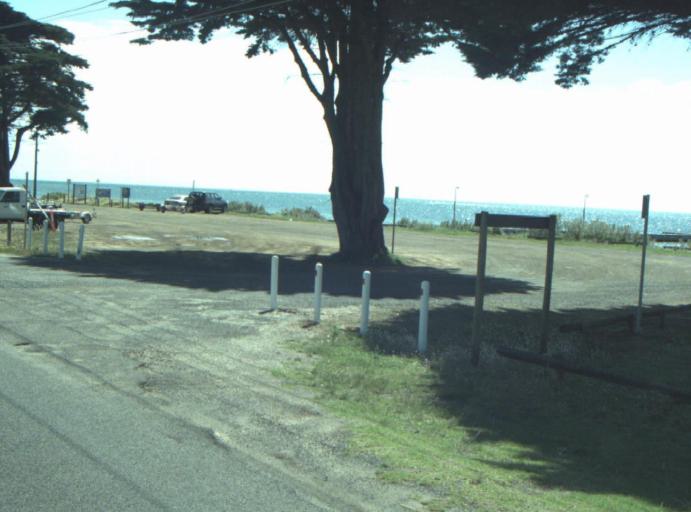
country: AU
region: Victoria
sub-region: Queenscliffe
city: Queenscliff
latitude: -38.1804
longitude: 144.7148
